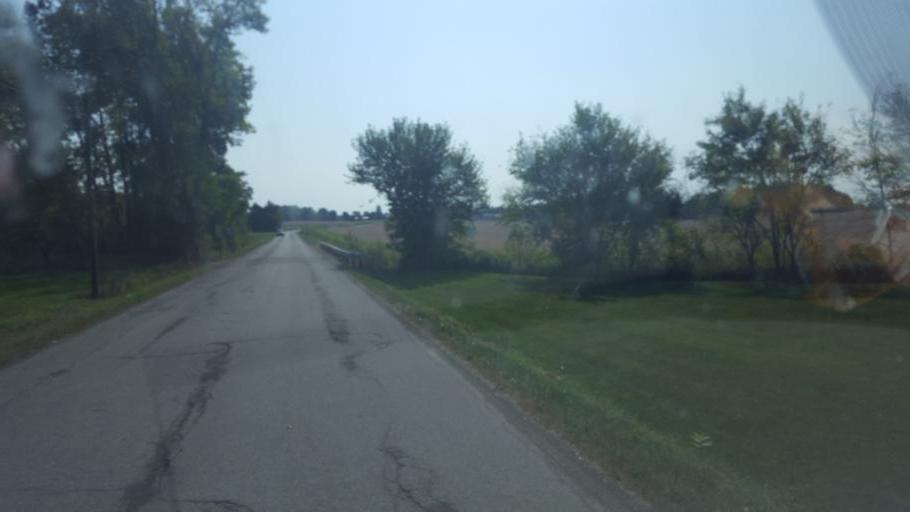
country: US
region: Ohio
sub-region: Crawford County
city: Galion
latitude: 40.6670
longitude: -82.8419
